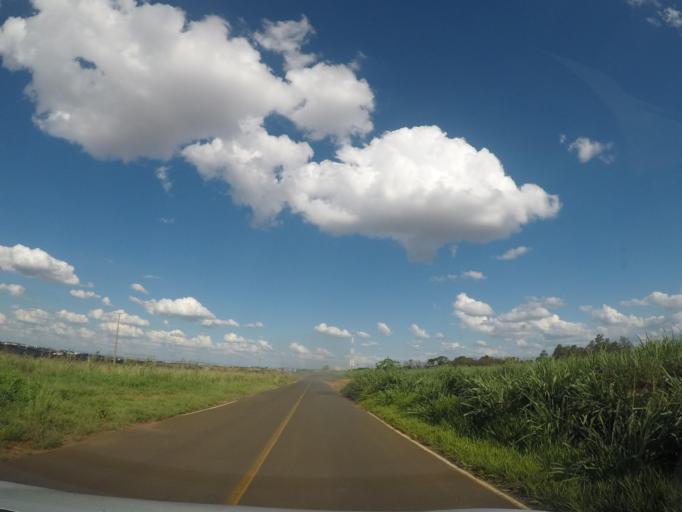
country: BR
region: Sao Paulo
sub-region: Sumare
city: Sumare
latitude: -22.8549
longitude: -47.3172
